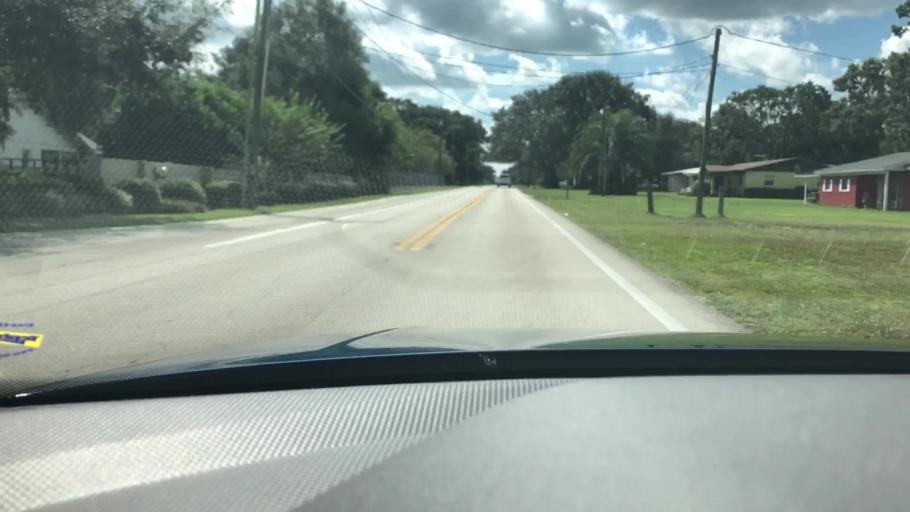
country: US
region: Florida
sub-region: Polk County
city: Gibsonia
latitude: 28.1423
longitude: -81.9384
